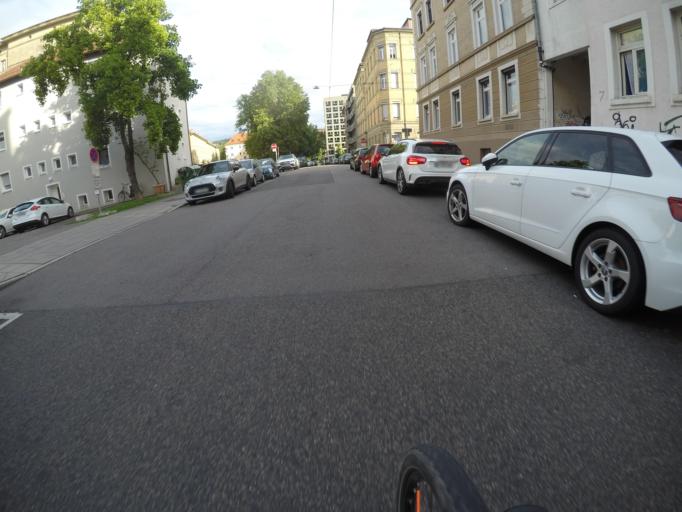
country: DE
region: Baden-Wuerttemberg
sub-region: Regierungsbezirk Stuttgart
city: Stuttgart
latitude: 48.7748
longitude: 9.1672
